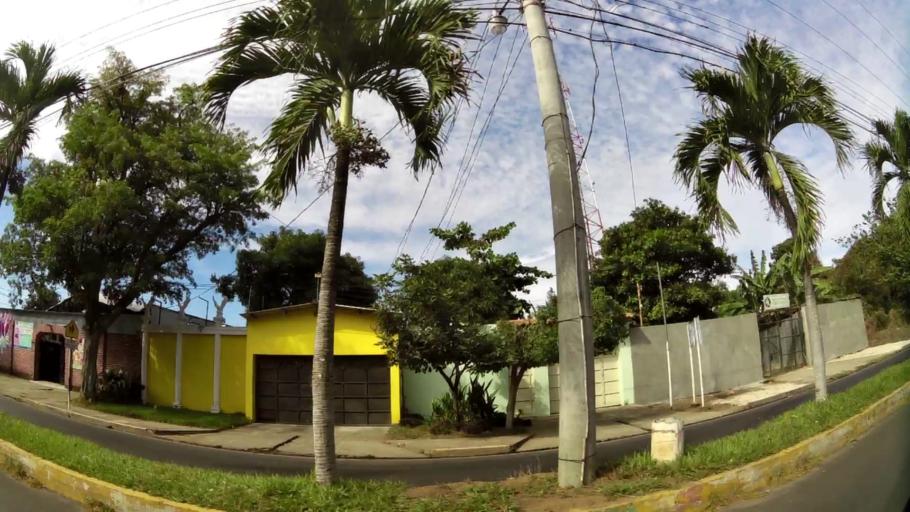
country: SV
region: Santa Ana
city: Chalchuapa
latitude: 13.9860
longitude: -89.6724
